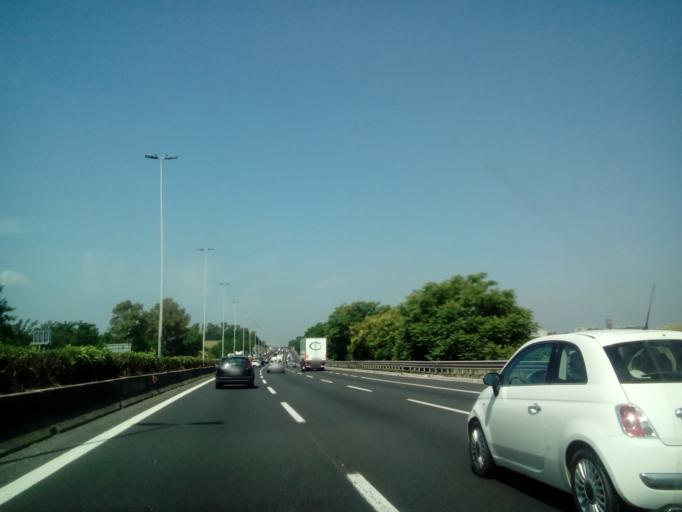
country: IT
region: Latium
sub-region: Citta metropolitana di Roma Capitale
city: Selcetta
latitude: 41.7943
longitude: 12.5086
